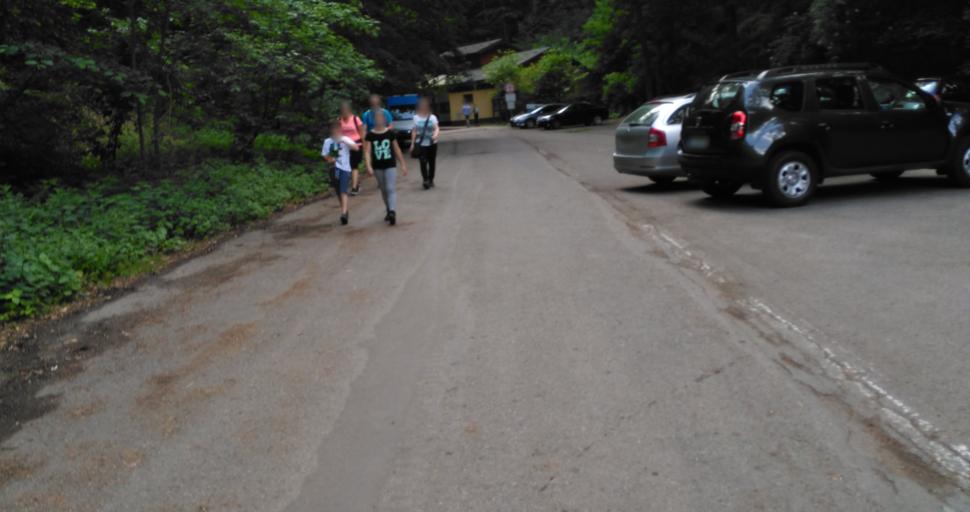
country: CZ
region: South Moravian
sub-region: Okres Blansko
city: Jedovnice
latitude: 49.3614
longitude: 16.7097
